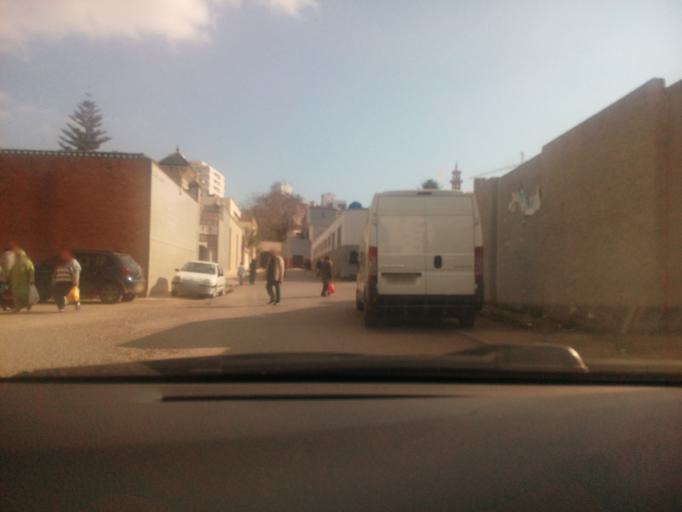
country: DZ
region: Oran
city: Oran
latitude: 35.7084
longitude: -0.6240
